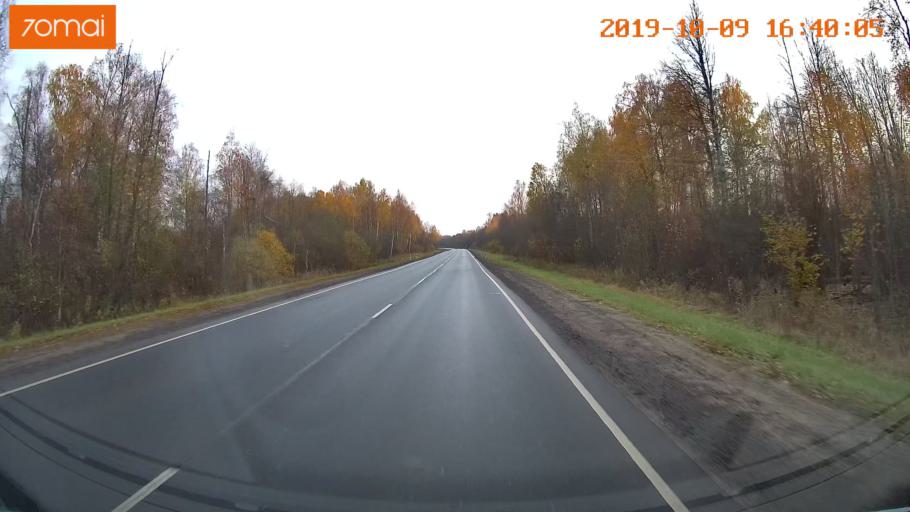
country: RU
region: Kostroma
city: Volgorechensk
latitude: 57.4887
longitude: 41.0562
